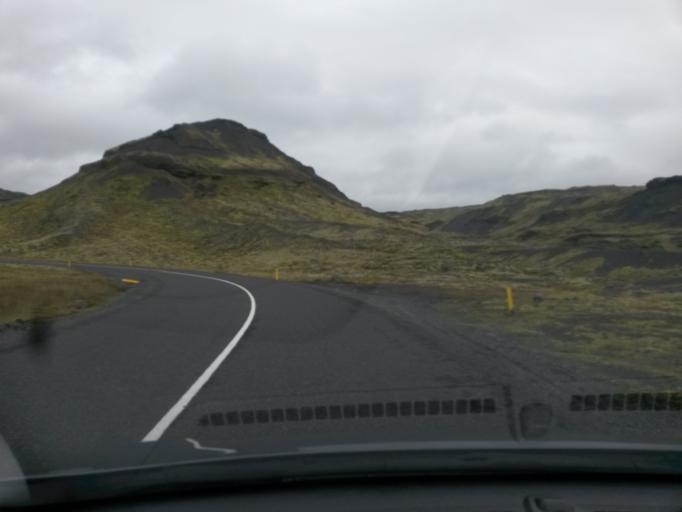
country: IS
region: South
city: Vestmannaeyjar
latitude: 63.5262
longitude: -19.3680
